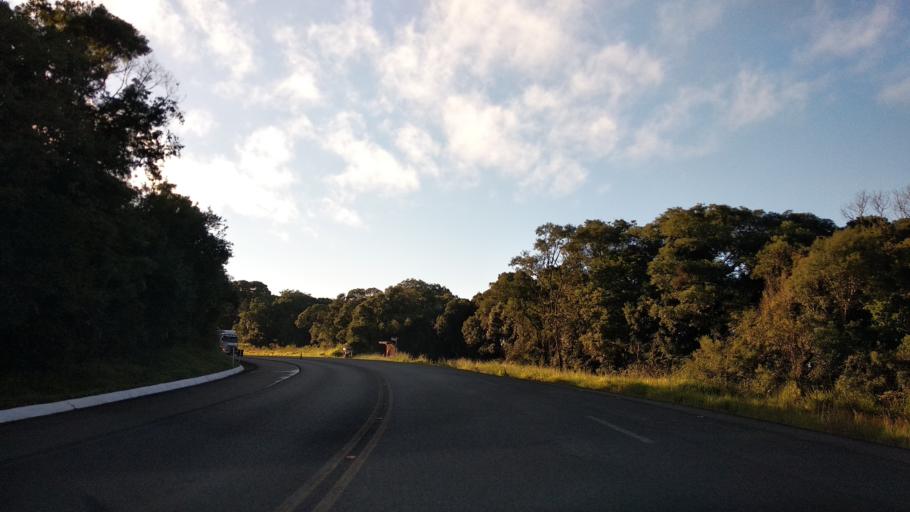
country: BR
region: Santa Catarina
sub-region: Curitibanos
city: Curitibanos
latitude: -27.6142
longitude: -50.7170
